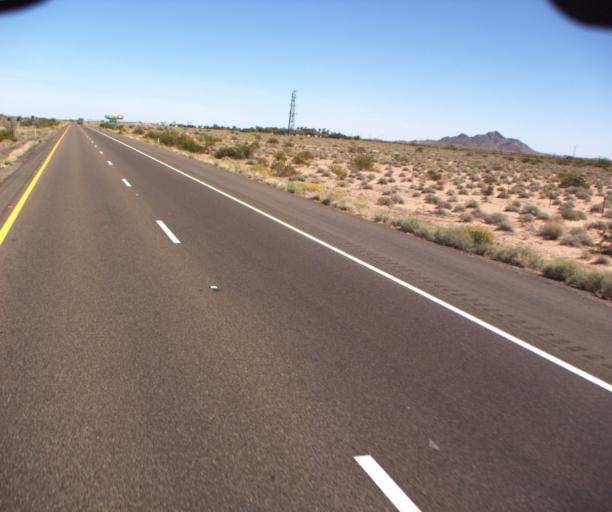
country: US
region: Arizona
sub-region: Yuma County
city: Wellton
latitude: 32.7928
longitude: -113.5544
